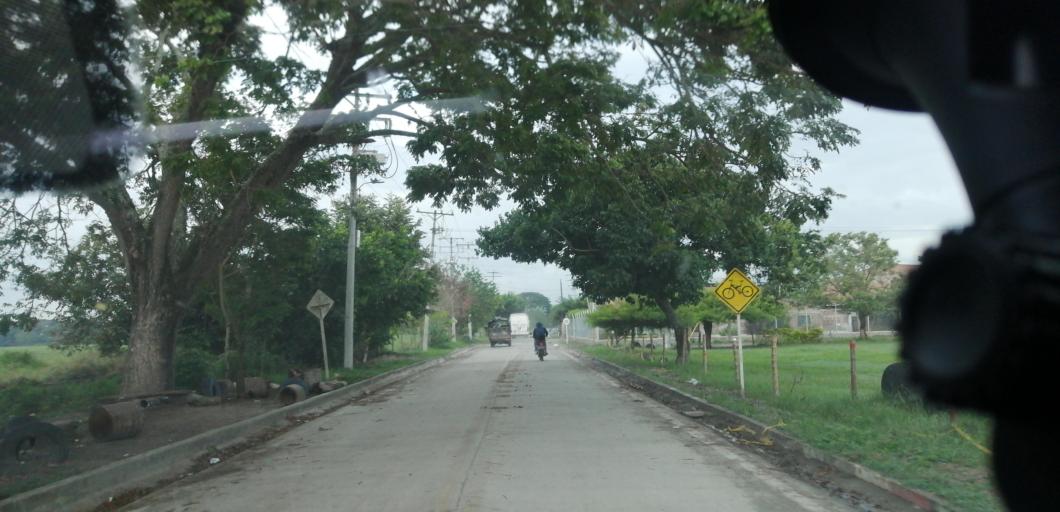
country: CO
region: Valle del Cauca
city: Yumbo
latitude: 3.5739
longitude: -76.4045
